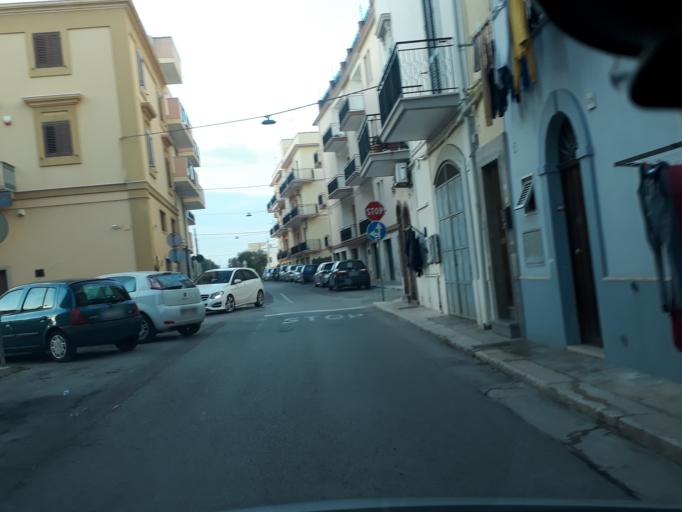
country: IT
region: Apulia
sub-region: Provincia di Brindisi
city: Fasano
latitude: 40.8385
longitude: 17.3558
